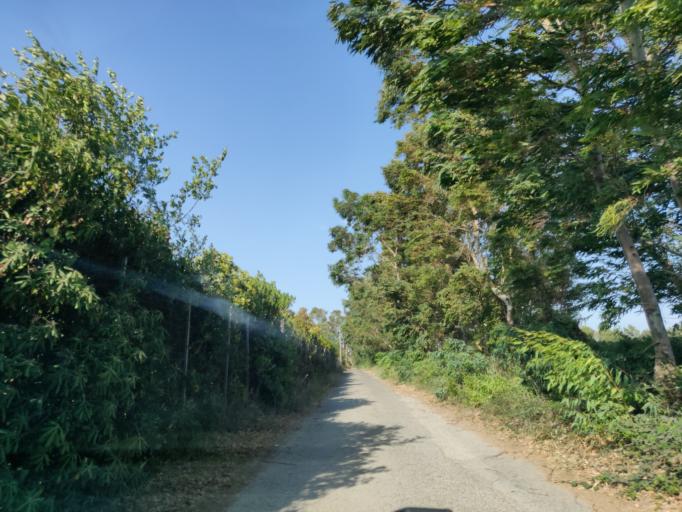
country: IT
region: Latium
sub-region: Citta metropolitana di Roma Capitale
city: Aurelia
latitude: 42.1375
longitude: 11.7614
